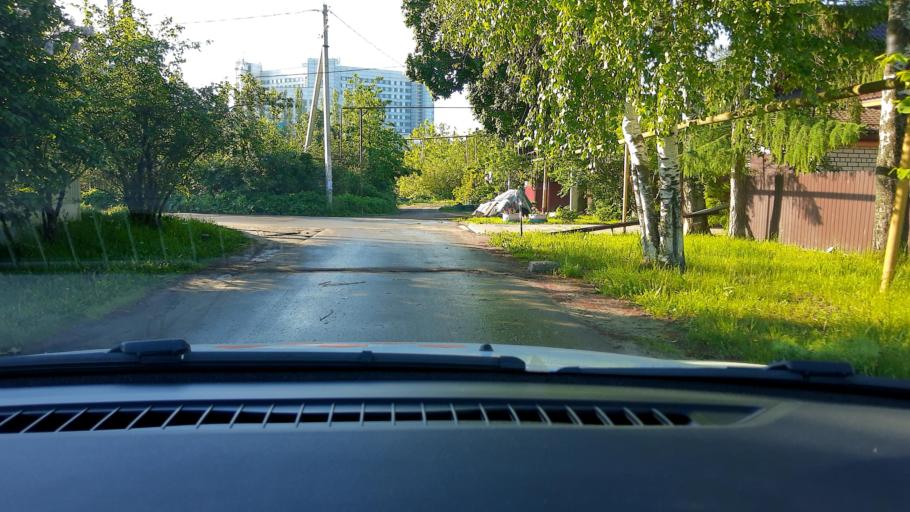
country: RU
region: Nizjnij Novgorod
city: Burevestnik
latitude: 56.2219
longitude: 43.8263
